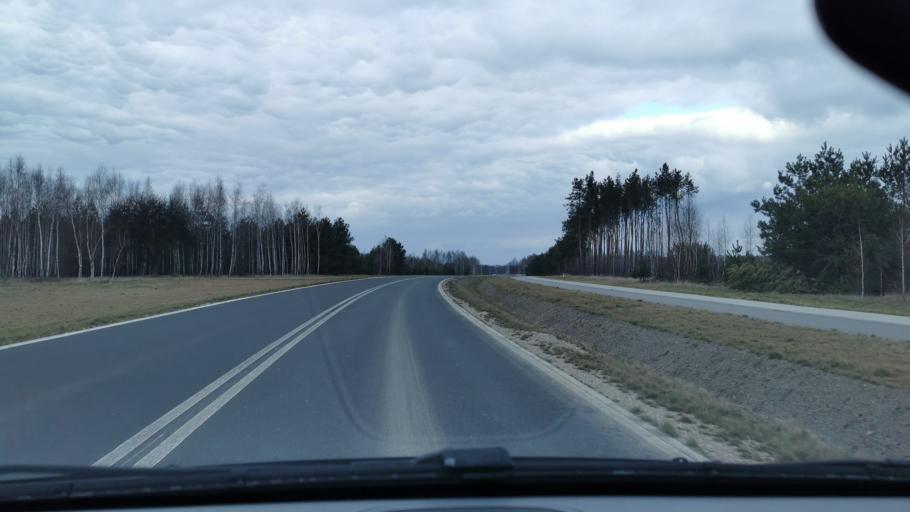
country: PL
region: Masovian Voivodeship
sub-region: Powiat zyrardowski
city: Zyrardow
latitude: 51.9978
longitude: 20.4636
